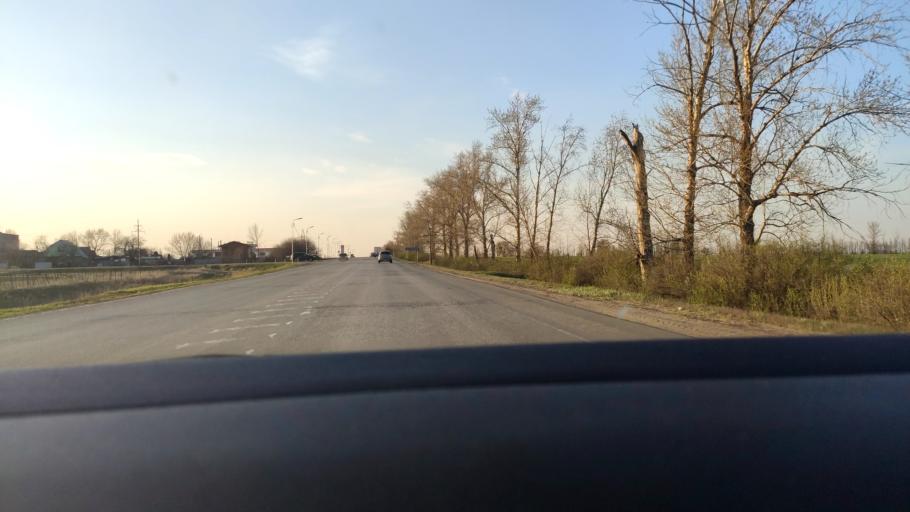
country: RU
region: Voronezj
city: Maslovka
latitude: 51.5034
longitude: 39.3083
